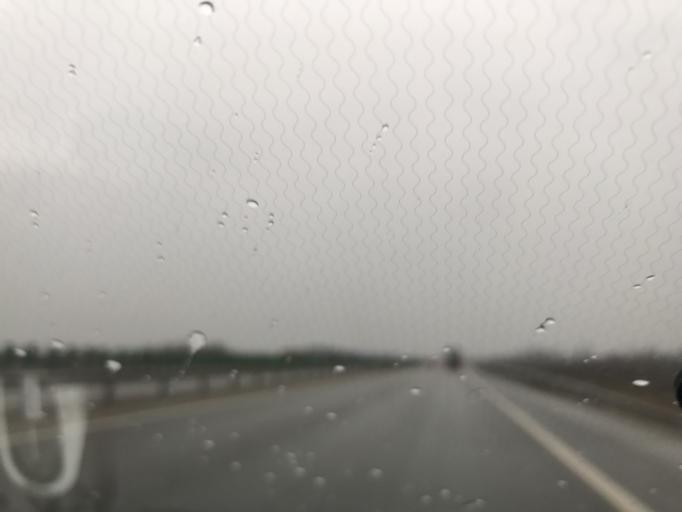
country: RU
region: Krasnodarskiy
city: Krylovskaya
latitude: 46.2912
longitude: 39.8231
